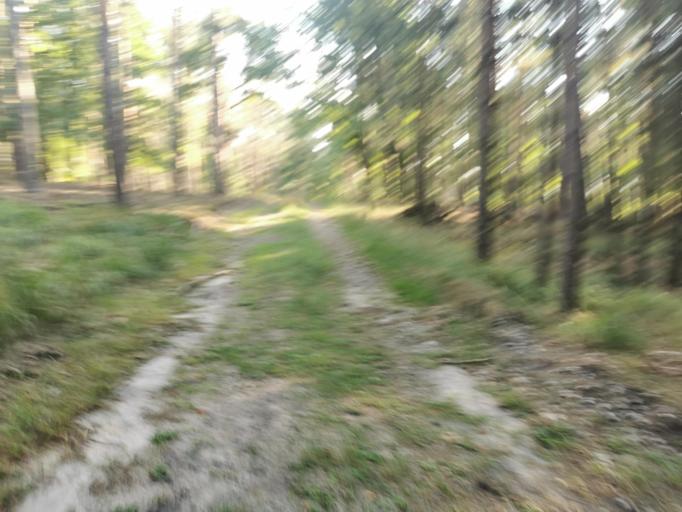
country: SK
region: Trnavsky
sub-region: Okres Senica
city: Senica
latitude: 48.6366
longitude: 17.2941
